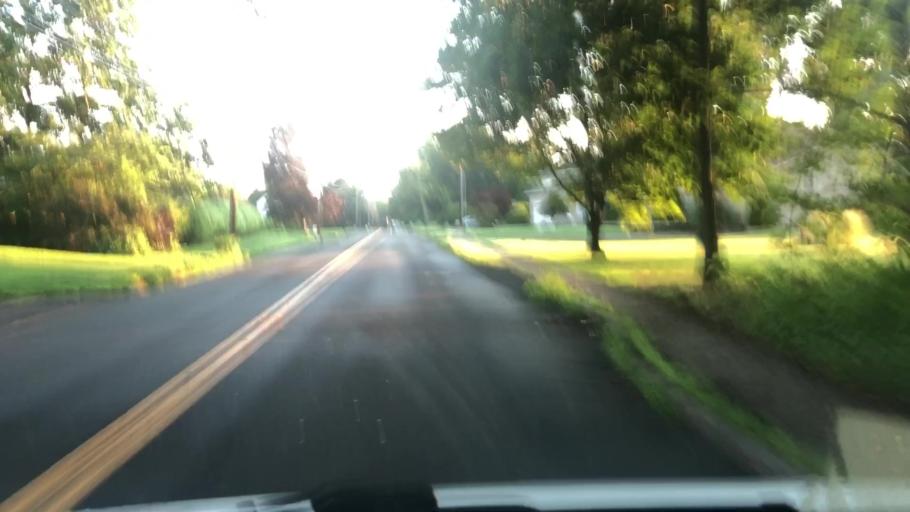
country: US
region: Massachusetts
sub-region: Hampshire County
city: Easthampton
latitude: 42.2699
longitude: -72.6686
